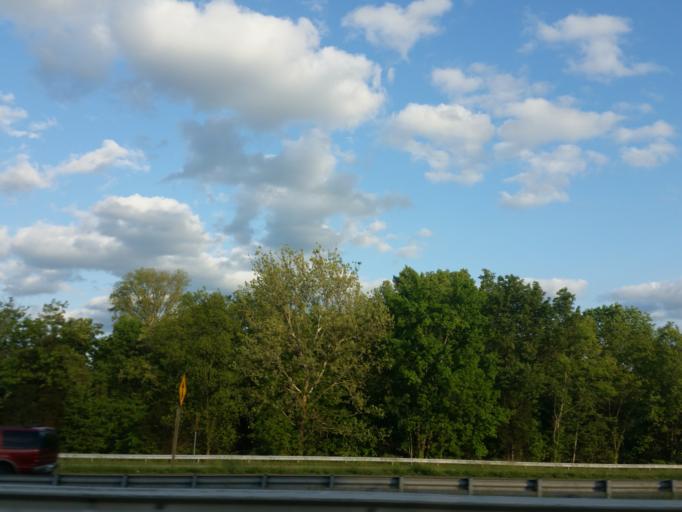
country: US
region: Virginia
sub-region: Washington County
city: Abingdon
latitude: 36.6787
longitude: -82.0391
